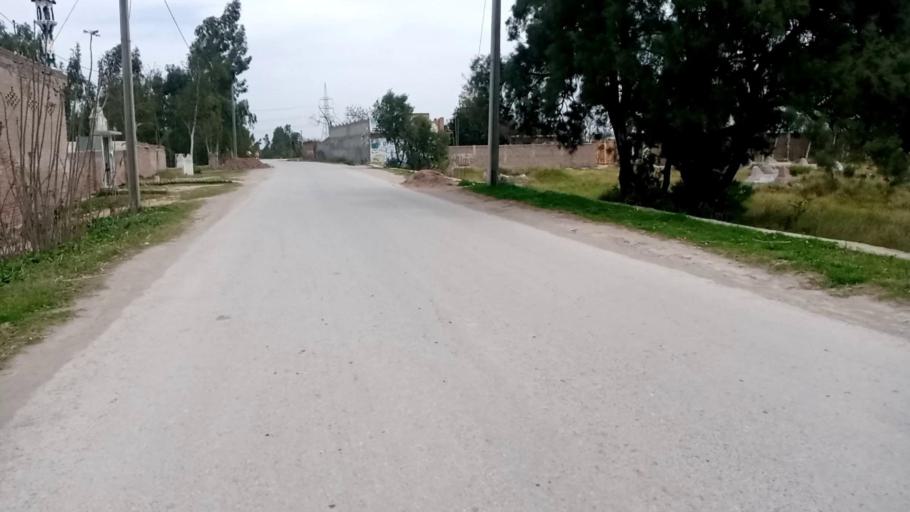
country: PK
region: Khyber Pakhtunkhwa
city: Charsadda
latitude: 34.0632
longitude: 71.6889
